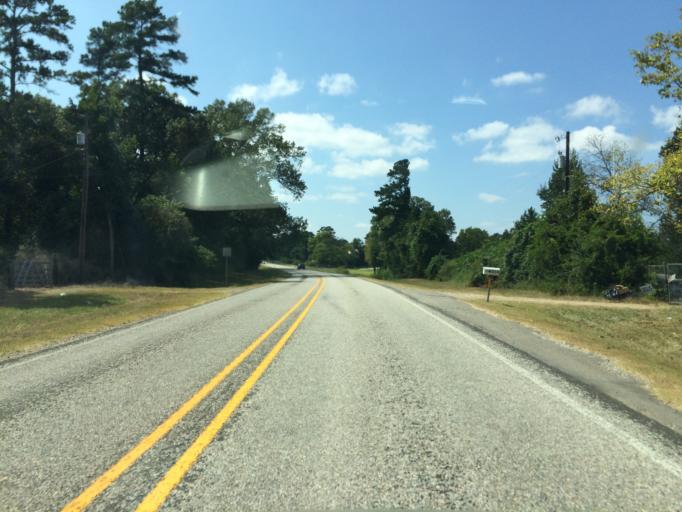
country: US
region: Texas
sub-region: Wood County
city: Hawkins
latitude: 32.6476
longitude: -95.2398
